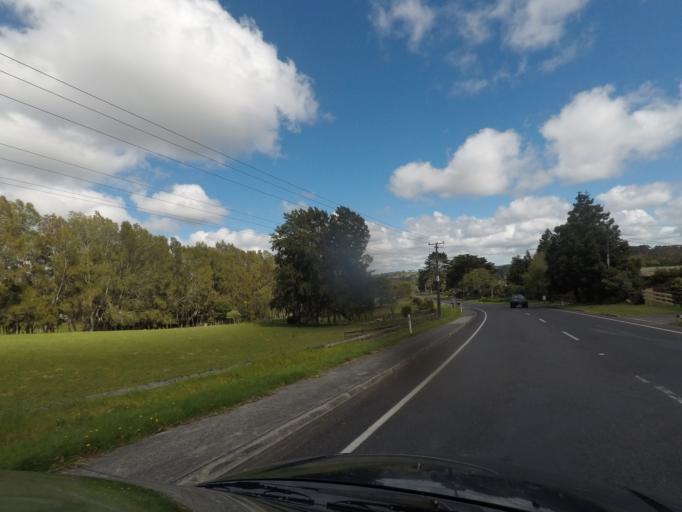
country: NZ
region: Auckland
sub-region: Auckland
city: Rothesay Bay
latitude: -36.7596
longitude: 174.6550
